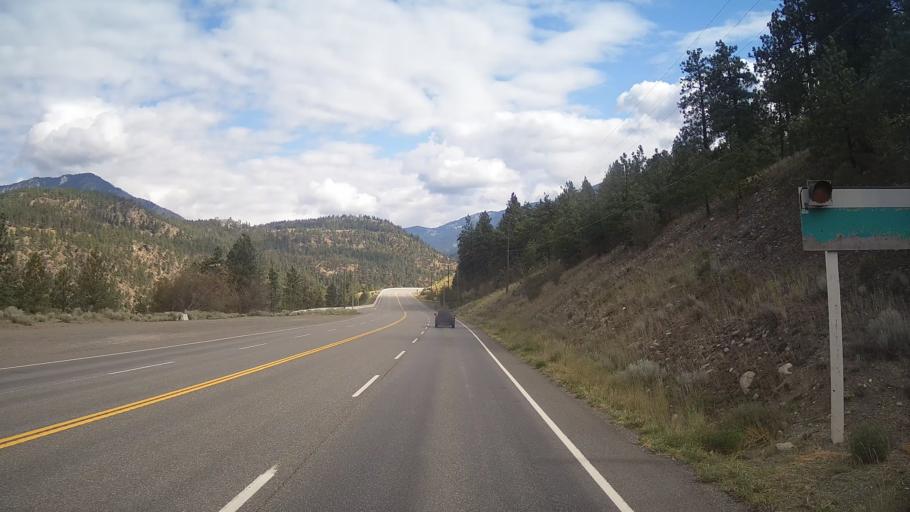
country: CA
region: British Columbia
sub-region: Thompson-Nicola Regional District
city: Ashcroft
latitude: 50.2395
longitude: -121.5740
